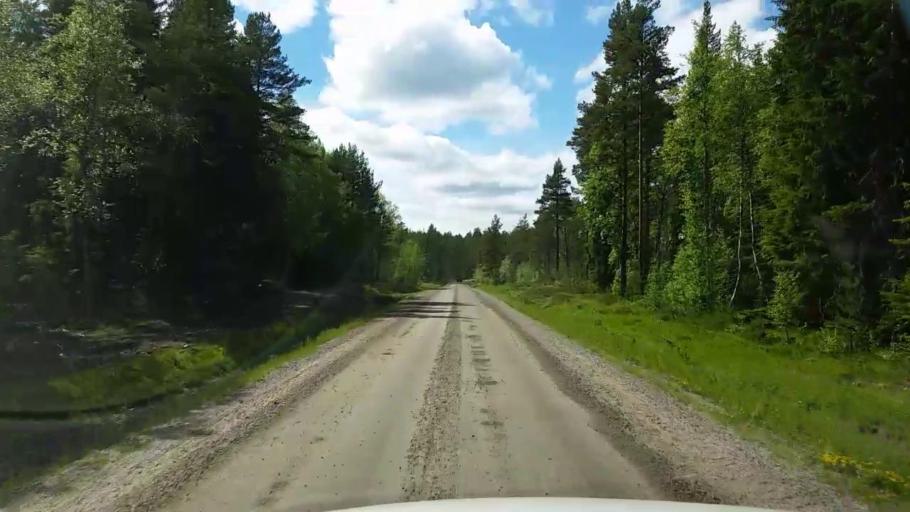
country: SE
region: Gaevleborg
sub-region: Ovanakers Kommun
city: Edsbyn
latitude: 61.5712
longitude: 15.9421
